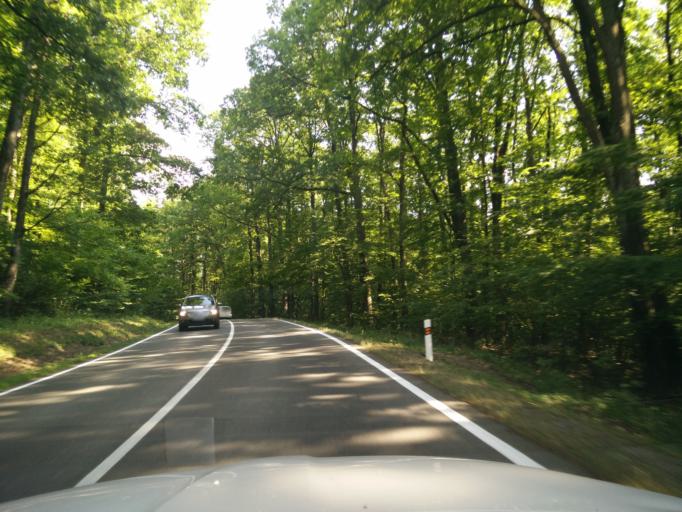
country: SK
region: Nitriansky
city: Bojnice
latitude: 48.7902
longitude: 18.5471
